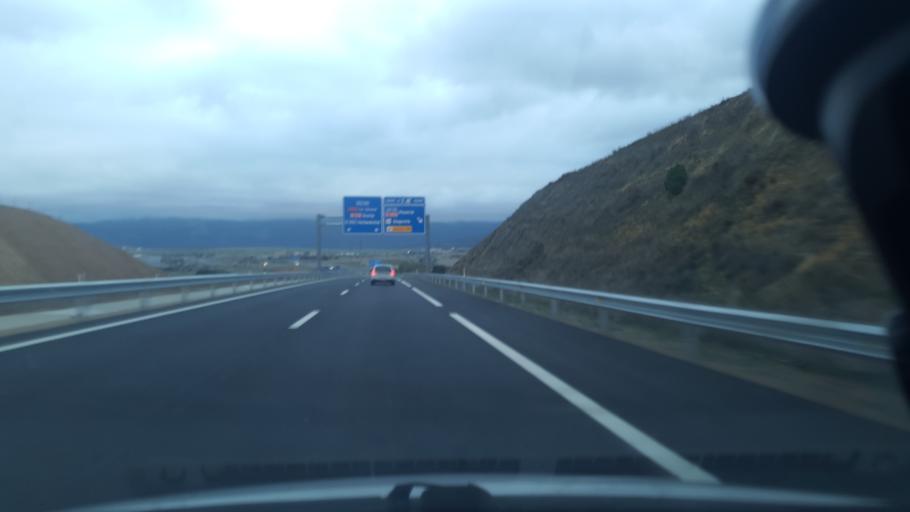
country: ES
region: Castille and Leon
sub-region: Provincia de Segovia
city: Segovia
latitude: 40.9202
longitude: -4.1308
